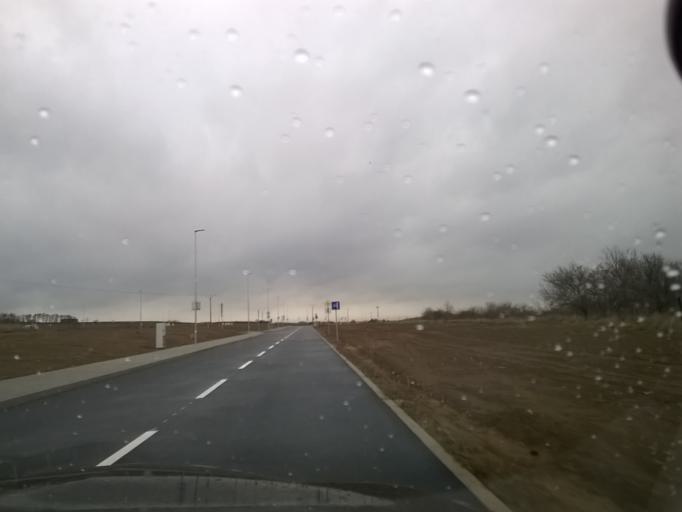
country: SK
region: Nitriansky
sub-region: Okres Nitra
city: Nitra
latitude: 48.3447
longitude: 18.0226
